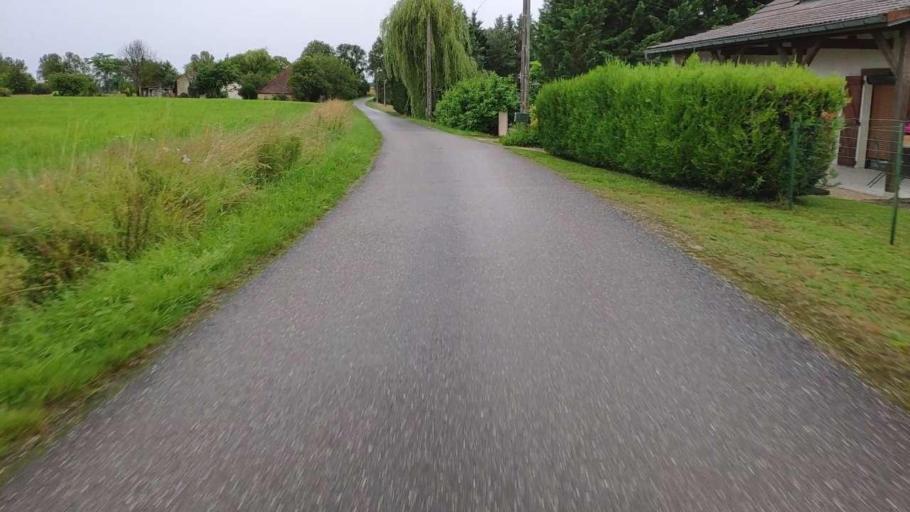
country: FR
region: Franche-Comte
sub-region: Departement du Jura
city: Chaussin
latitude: 46.8809
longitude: 5.4151
